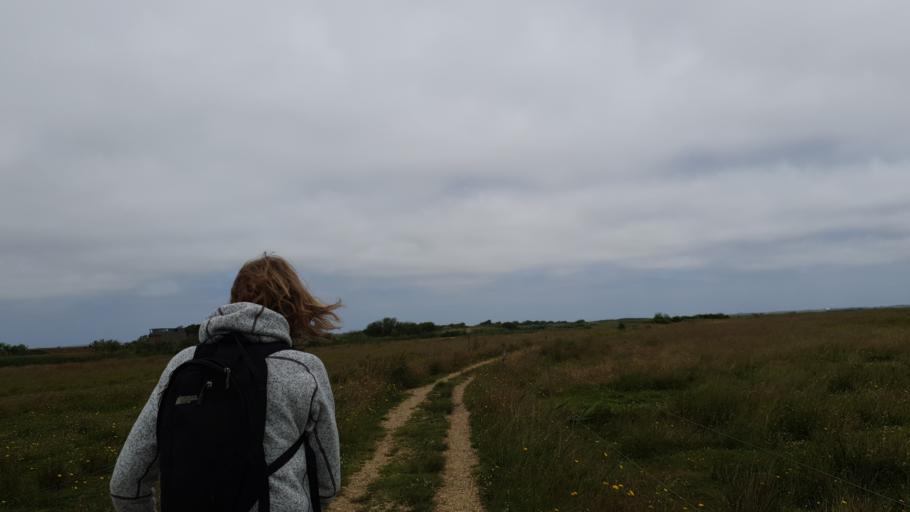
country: DK
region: Central Jutland
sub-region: Ringkobing-Skjern Kommune
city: Skjern
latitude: 55.9162
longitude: 8.4059
